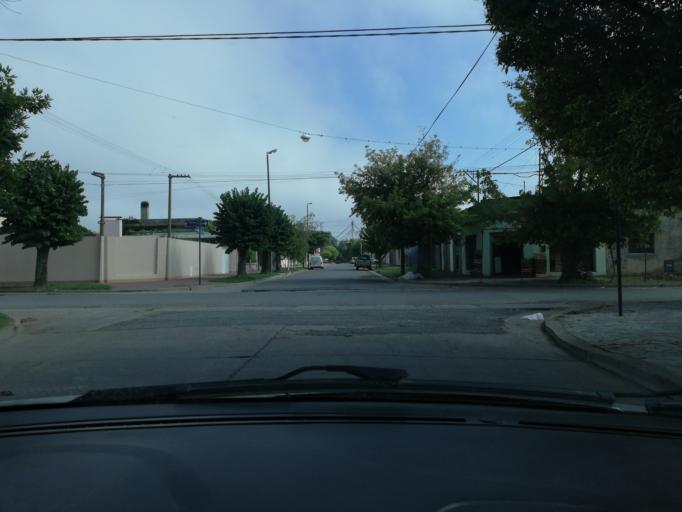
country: AR
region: Buenos Aires
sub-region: Partido de Balcarce
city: Balcarce
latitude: -37.8381
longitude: -58.2639
